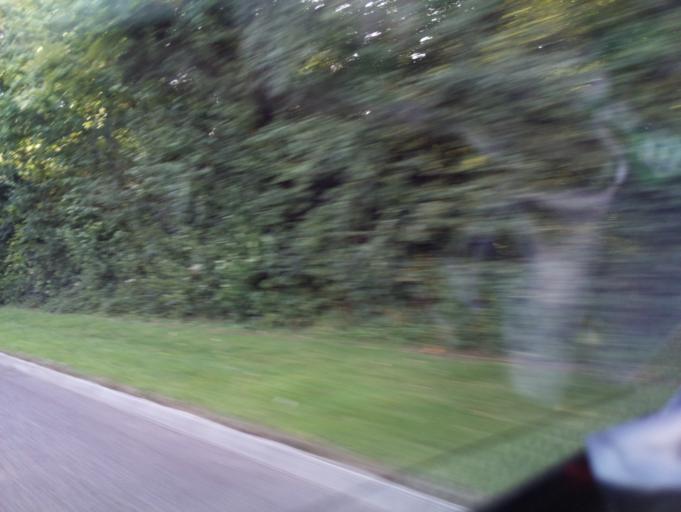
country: GB
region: Wales
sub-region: Torfaen County Borough
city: Cwmbran
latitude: 51.6402
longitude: -3.0036
